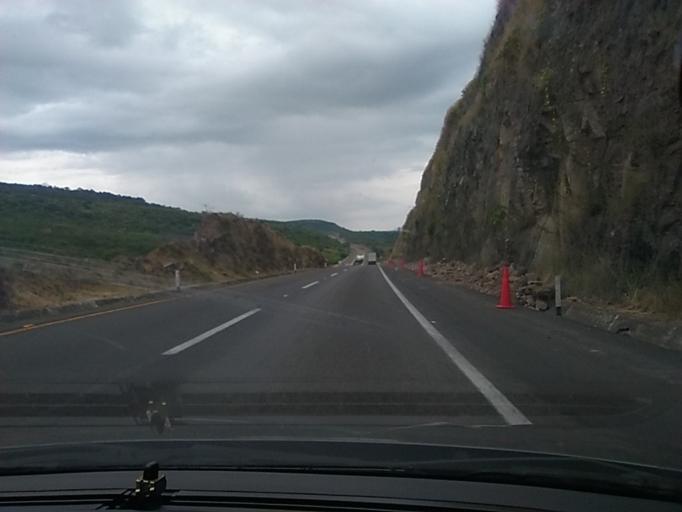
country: MX
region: Jalisco
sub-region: Zapotlan del Rey
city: Zapotlan del Rey
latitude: 20.4962
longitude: -102.9462
